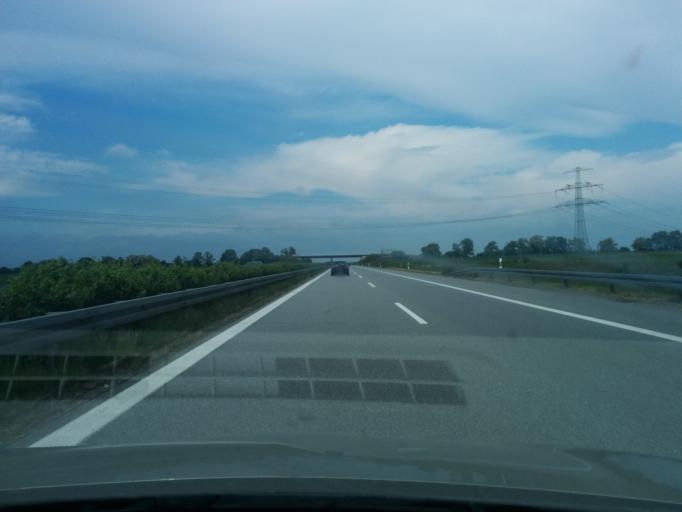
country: DE
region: Mecklenburg-Vorpommern
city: Kessin
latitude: 53.7445
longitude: 13.3347
